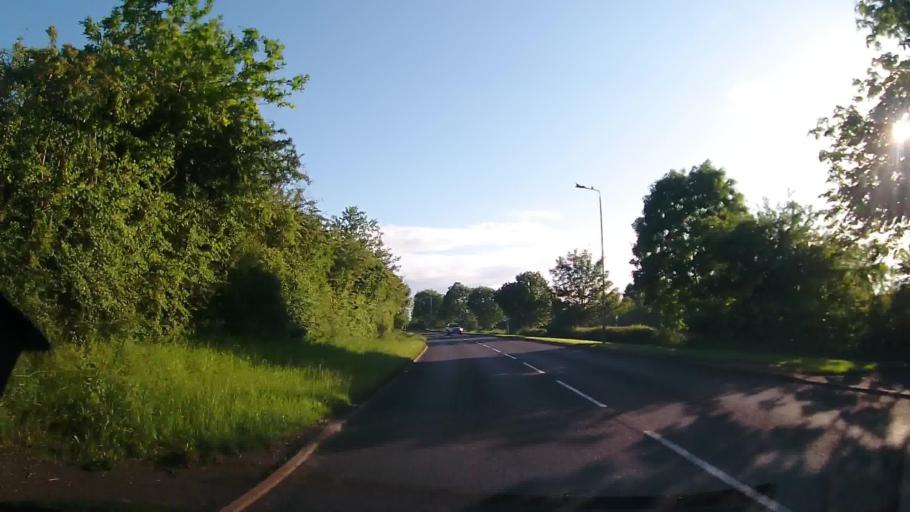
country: GB
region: England
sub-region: Leicestershire
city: Glenfield
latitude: 52.6597
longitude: -1.2117
